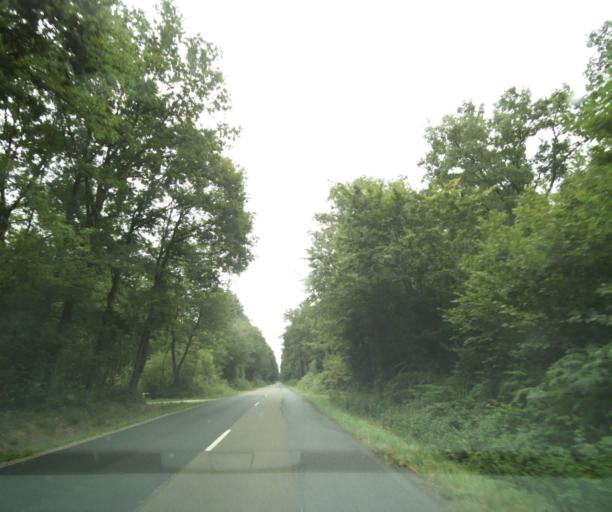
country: FR
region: Pays de la Loire
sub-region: Departement de la Sarthe
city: Precigne
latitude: 47.7421
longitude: -0.2815
